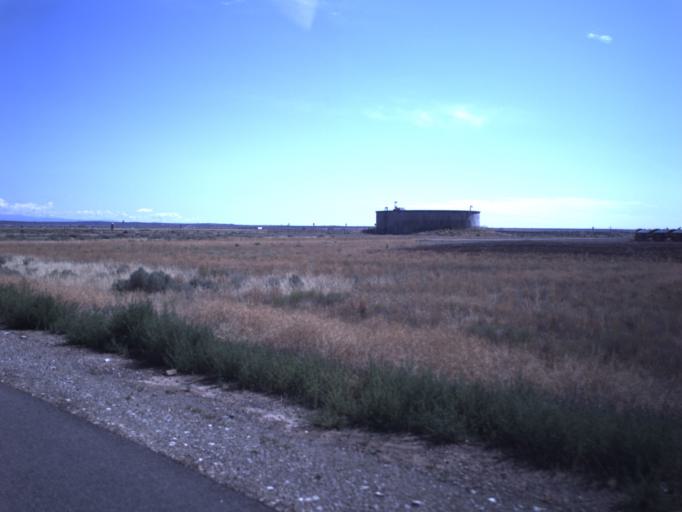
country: US
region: Utah
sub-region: Duchesne County
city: Duchesne
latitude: 40.1957
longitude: -110.3913
